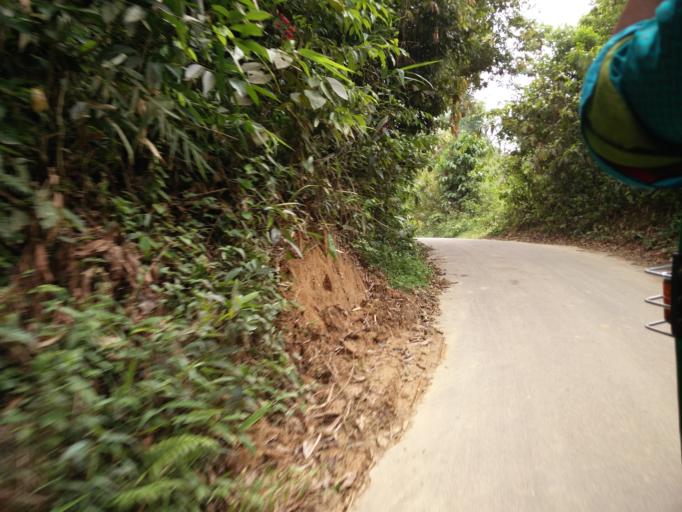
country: IN
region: Tripura
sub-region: Dhalai
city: Kamalpur
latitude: 24.3032
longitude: 91.7863
